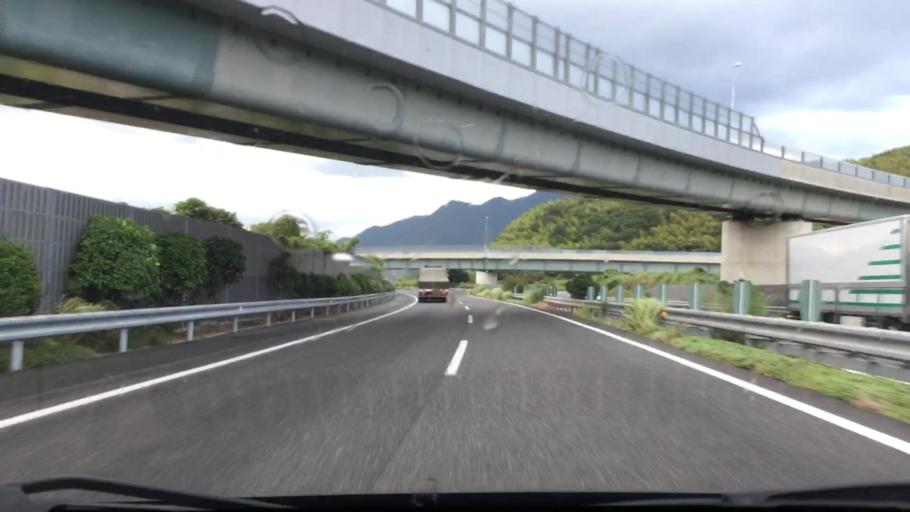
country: JP
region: Fukuoka
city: Kitakyushu
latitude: 33.8150
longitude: 130.8842
